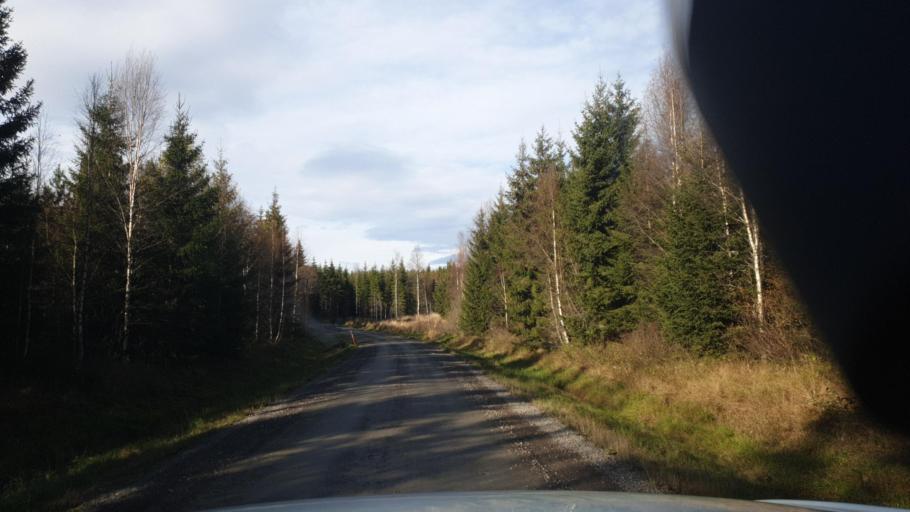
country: SE
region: Vaermland
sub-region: Eda Kommun
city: Charlottenberg
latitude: 59.9696
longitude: 12.5028
